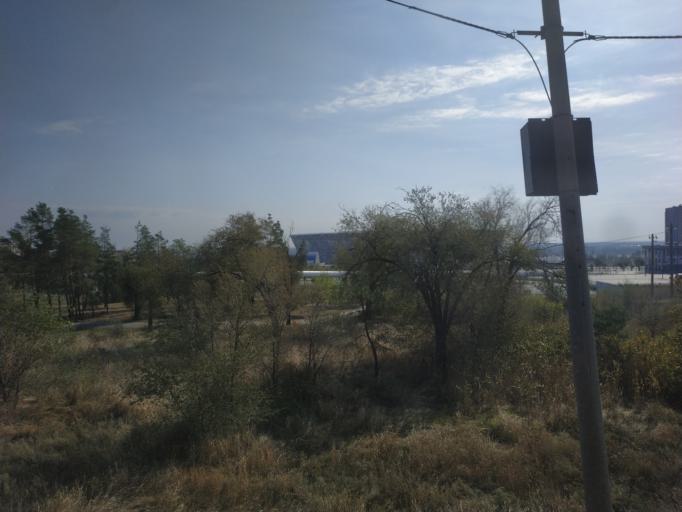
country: RU
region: Volgograd
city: Volgograd
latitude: 48.7374
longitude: 44.5405
